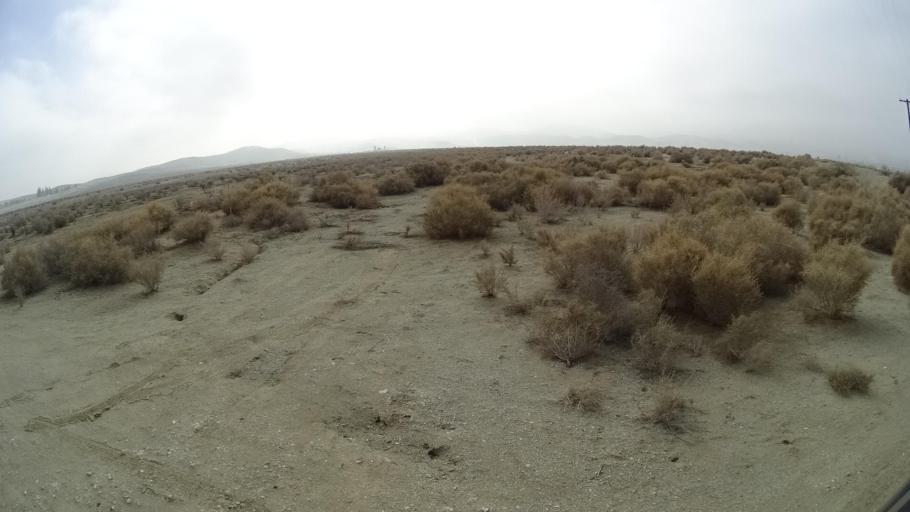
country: US
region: California
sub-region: Kern County
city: Maricopa
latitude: 35.0468
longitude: -119.3632
